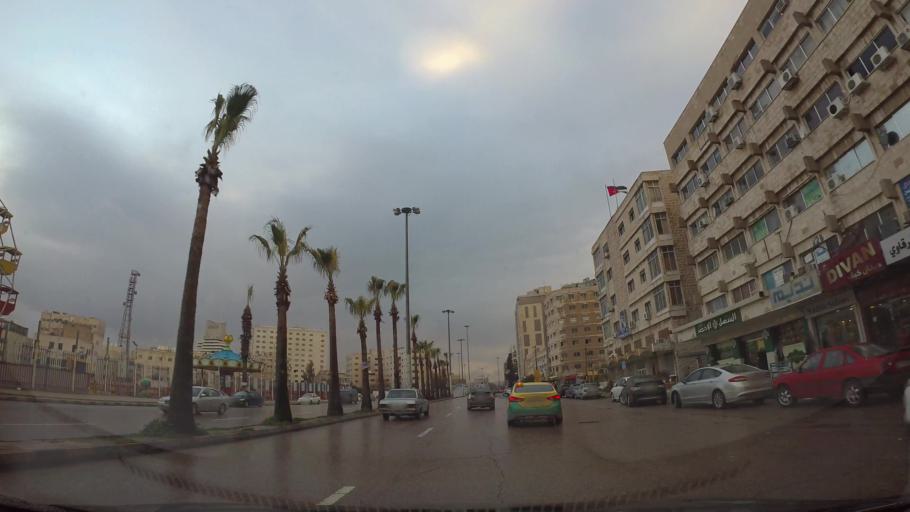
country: JO
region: Amman
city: Amman
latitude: 31.9711
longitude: 35.9128
